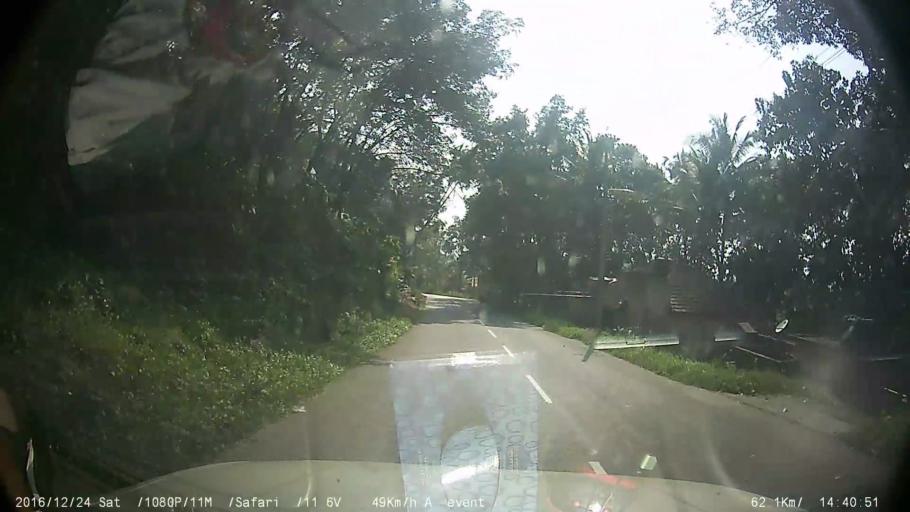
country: IN
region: Kerala
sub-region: Kottayam
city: Lalam
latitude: 9.7871
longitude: 76.7297
